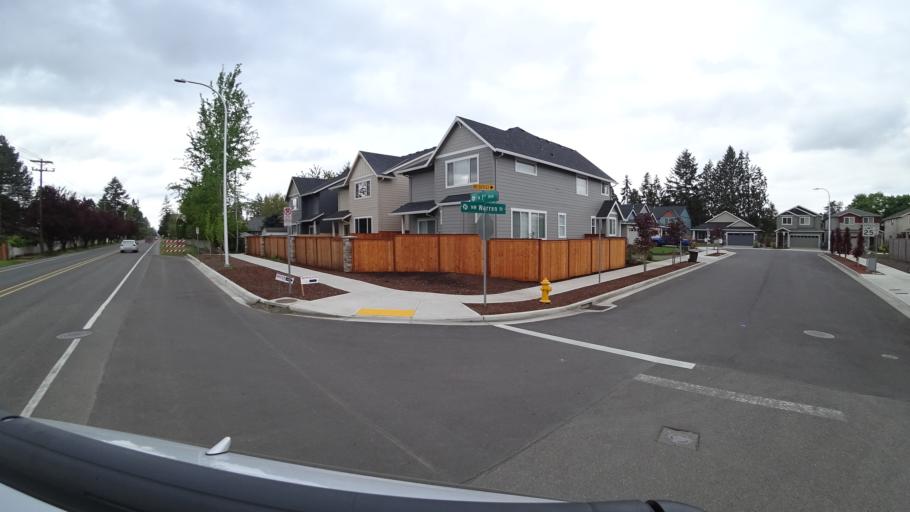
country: US
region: Oregon
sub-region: Washington County
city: Hillsboro
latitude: 45.5329
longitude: -122.9896
